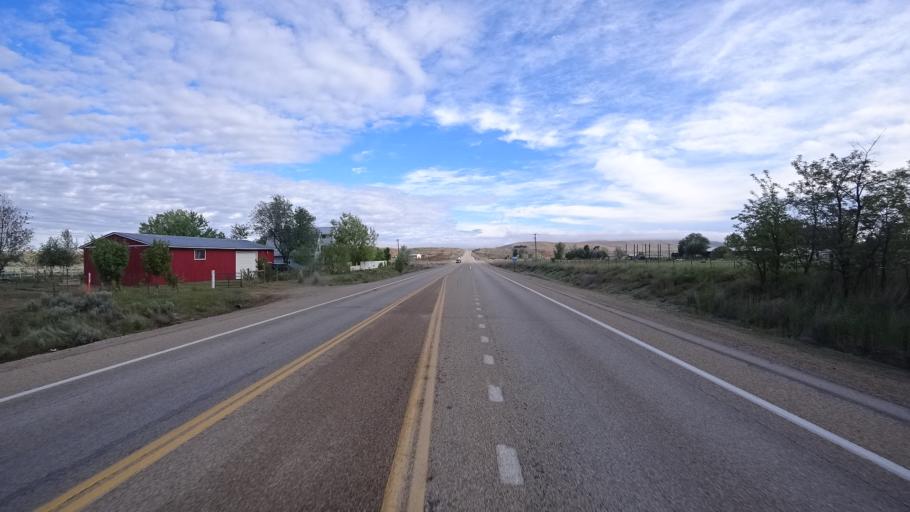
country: US
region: Idaho
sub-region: Ada County
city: Star
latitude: 43.7779
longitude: -116.4721
